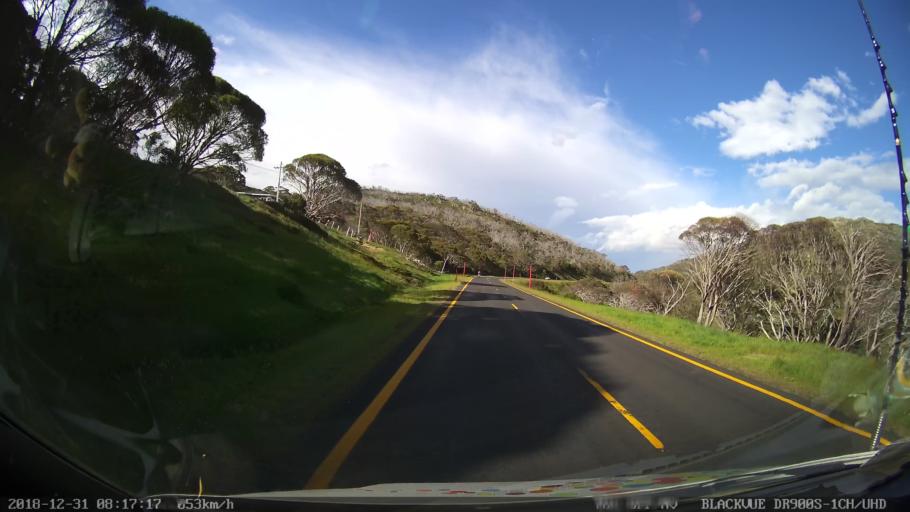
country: AU
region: New South Wales
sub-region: Snowy River
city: Jindabyne
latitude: -36.4097
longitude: 148.4058
